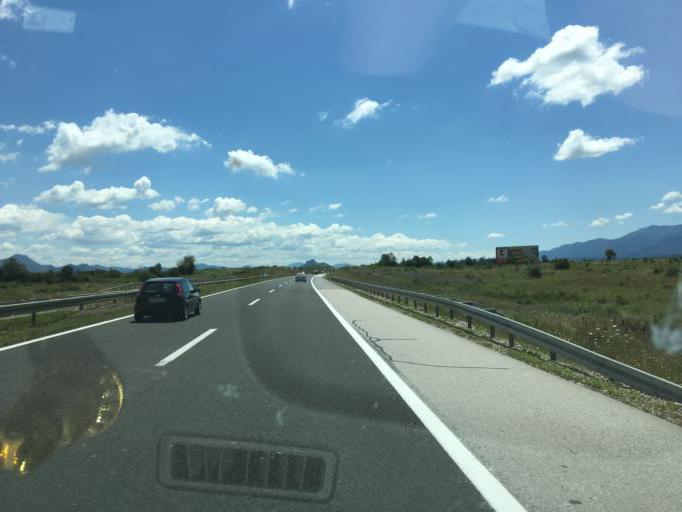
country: HR
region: Licko-Senjska
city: Gospic
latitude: 44.5026
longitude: 15.5295
